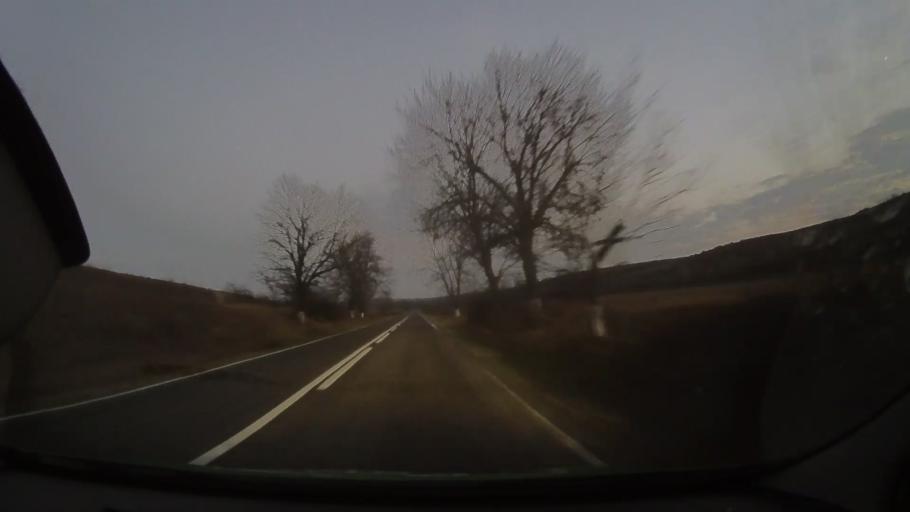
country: RO
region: Constanta
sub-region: Comuna Ion Corvin
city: Ion Corvin
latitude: 44.1096
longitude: 27.7755
